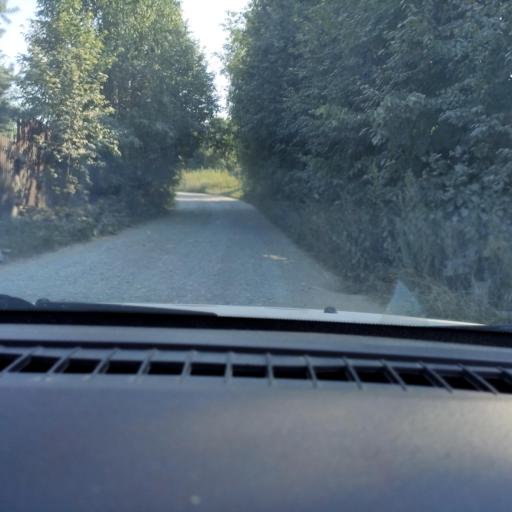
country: RU
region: Perm
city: Polazna
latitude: 58.1407
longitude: 56.4569
